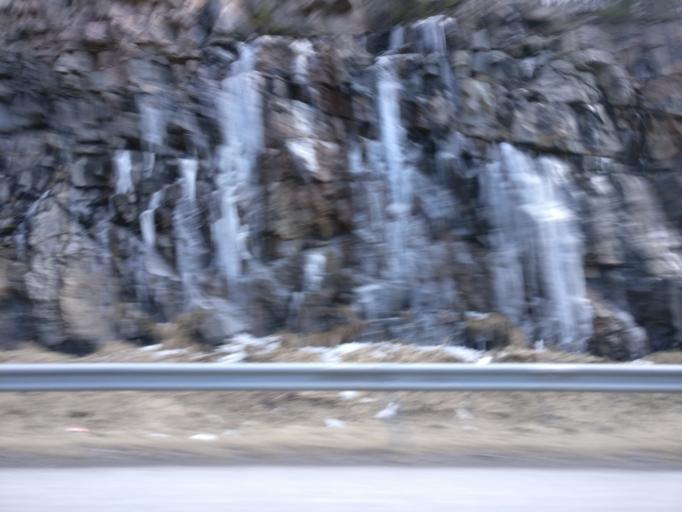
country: FI
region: Haeme
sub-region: Riihimaeki
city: Riihimaeki
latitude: 60.7463
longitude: 24.7301
